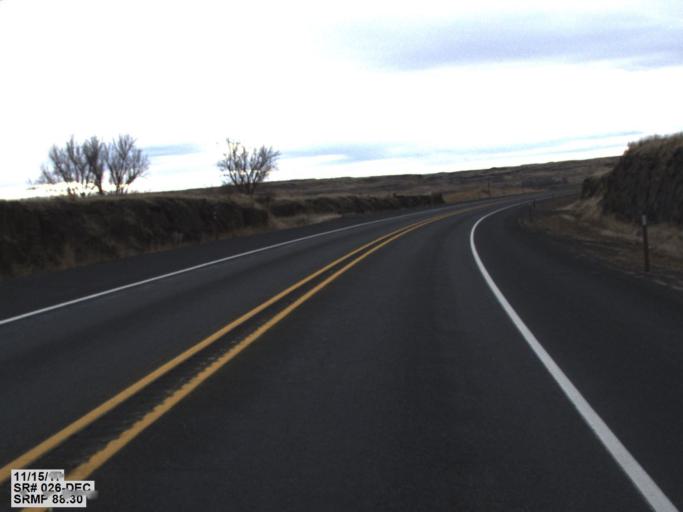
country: US
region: Washington
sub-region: Adams County
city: Ritzville
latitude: 46.7456
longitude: -118.2035
